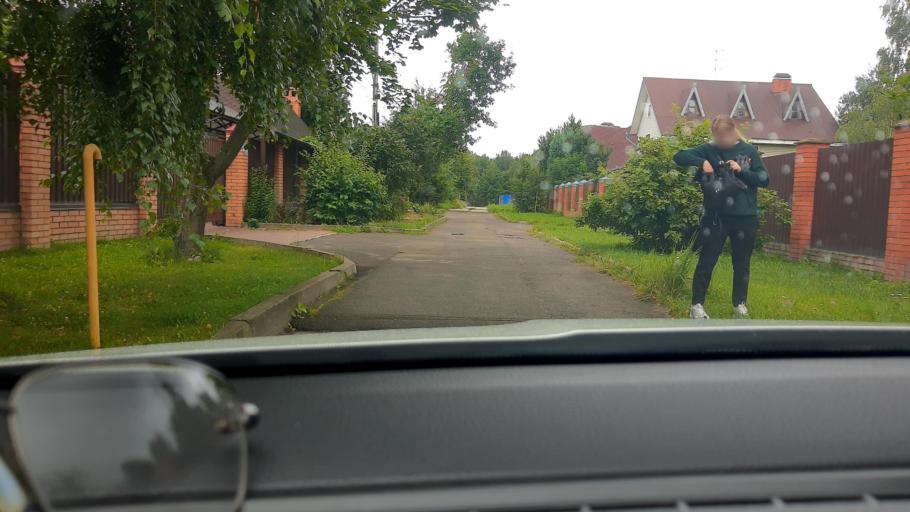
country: RU
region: Moskovskaya
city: Dolgoprudnyy
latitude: 55.9504
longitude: 37.4568
